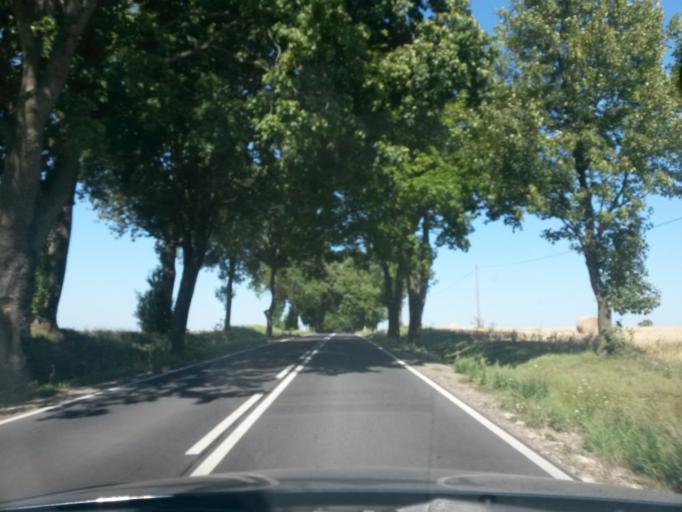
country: PL
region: Warmian-Masurian Voivodeship
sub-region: Powiat ilawski
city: Lubawa
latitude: 53.4039
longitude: 19.7996
